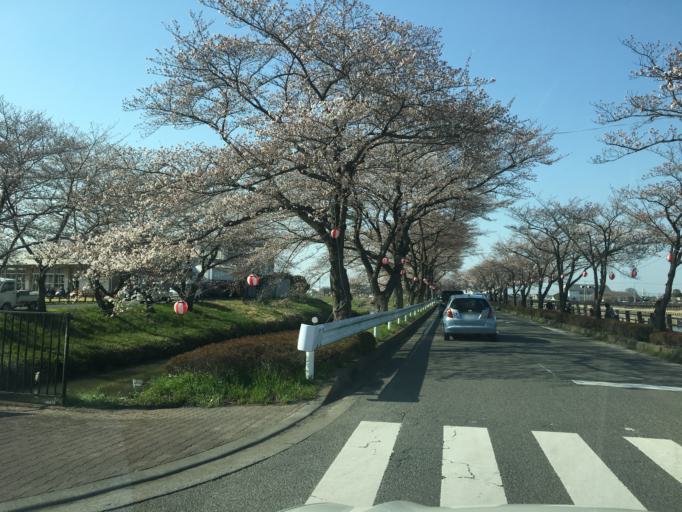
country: JP
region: Saitama
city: Kawagoe
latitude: 35.9241
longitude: 139.5144
